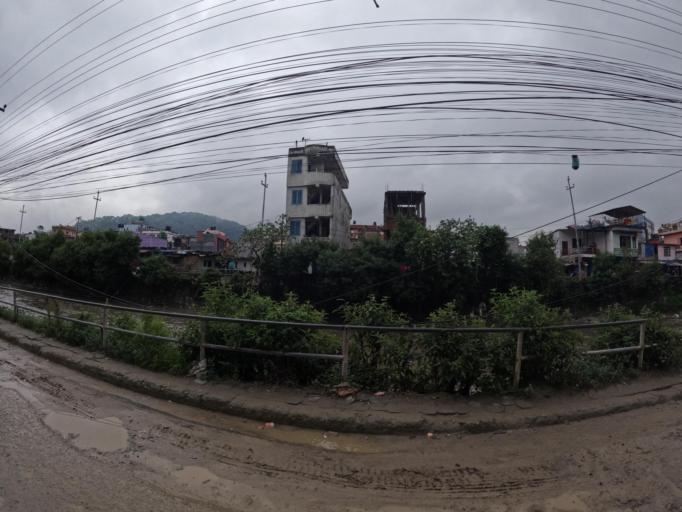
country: NP
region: Central Region
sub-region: Bagmati Zone
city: Kathmandu
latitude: 27.7380
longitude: 85.3095
